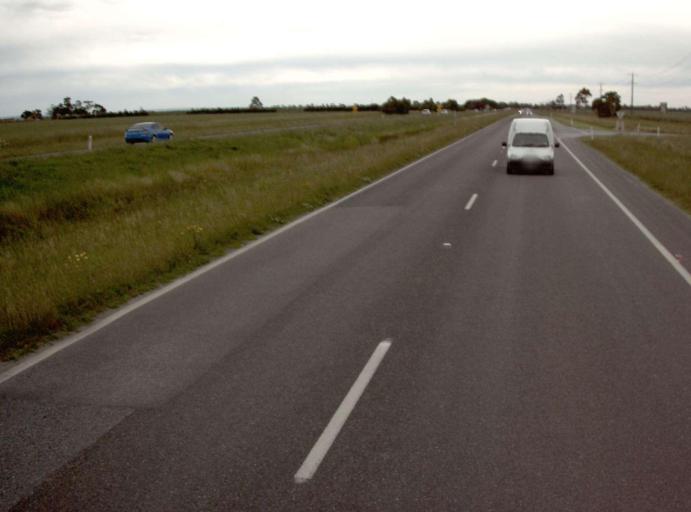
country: AU
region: Victoria
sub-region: Cardinia
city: Koo-Wee-Rup
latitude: -38.2423
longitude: 145.5292
